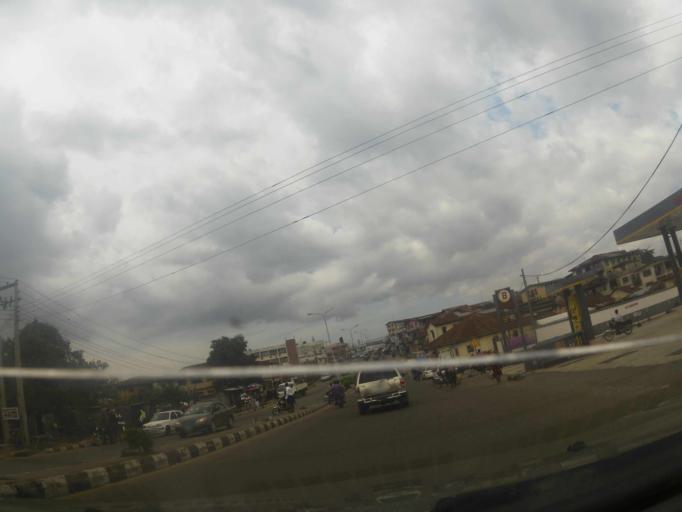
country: NG
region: Oyo
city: Ibadan
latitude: 7.3915
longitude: 3.8810
